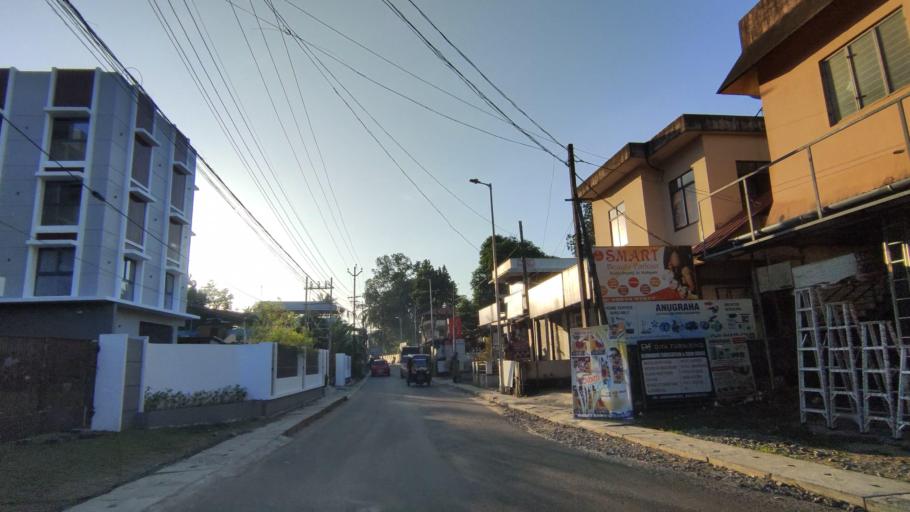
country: IN
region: Kerala
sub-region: Kottayam
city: Kottayam
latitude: 9.6125
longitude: 76.5074
